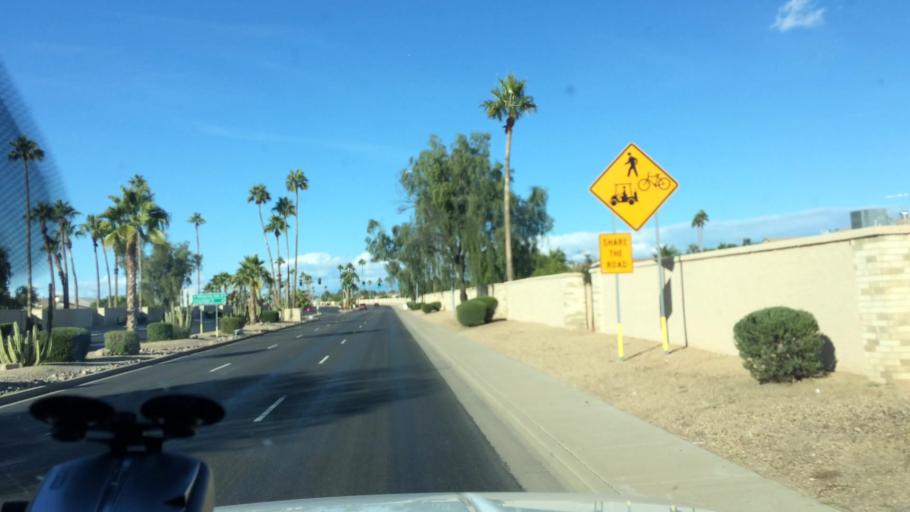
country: US
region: Arizona
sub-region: Maricopa County
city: Surprise
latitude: 33.6408
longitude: -112.3344
